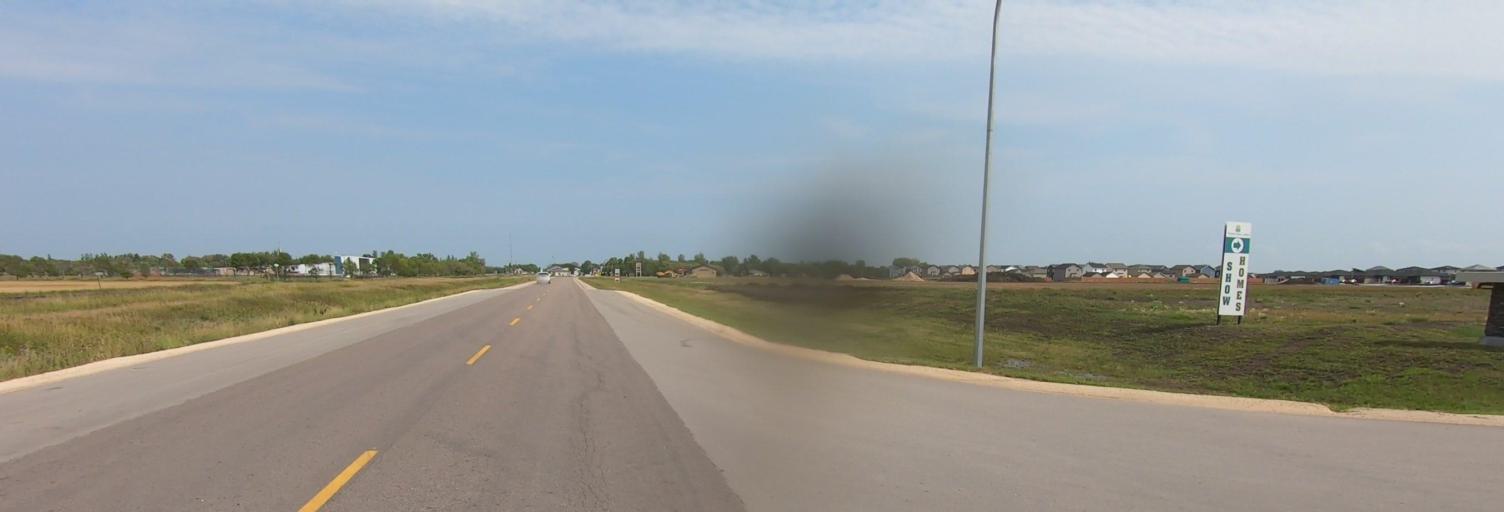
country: CA
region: Manitoba
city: Winnipeg
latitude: 49.6843
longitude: -97.2704
